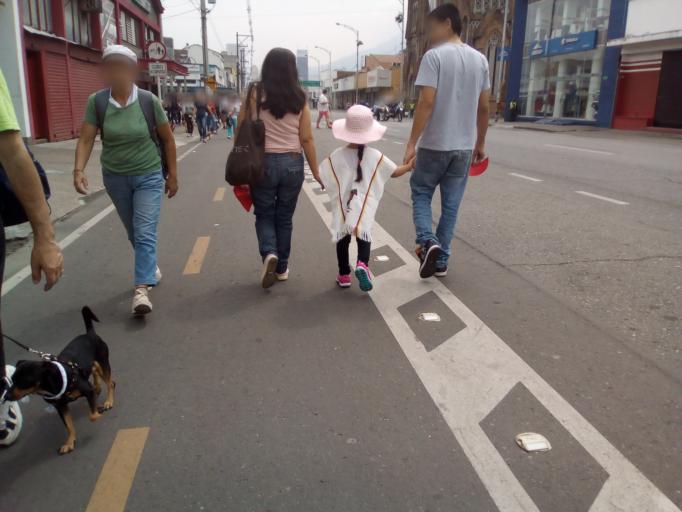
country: CO
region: Antioquia
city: Medellin
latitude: 6.2359
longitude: -75.5734
